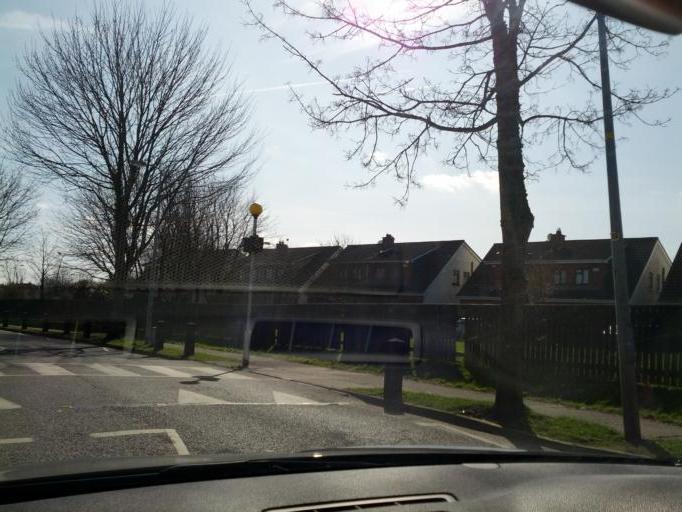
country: IE
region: Leinster
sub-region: Kildare
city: Maynooth
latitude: 53.3731
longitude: -6.5994
